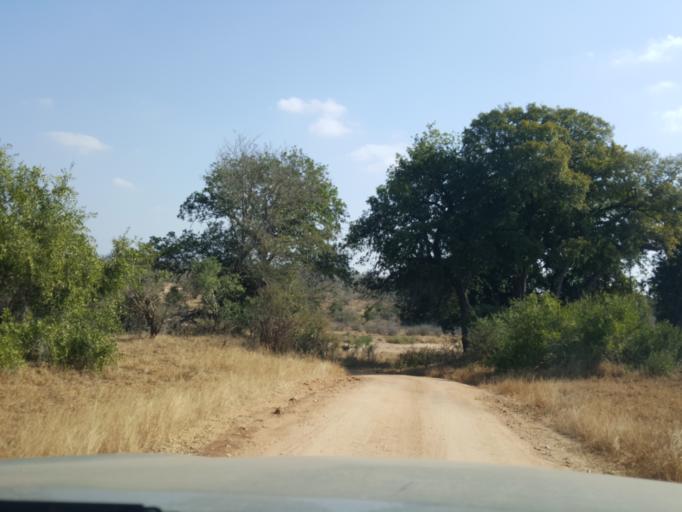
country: ZA
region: Mpumalanga
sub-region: Ehlanzeni District
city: Komatipoort
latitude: -25.2726
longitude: 31.7811
